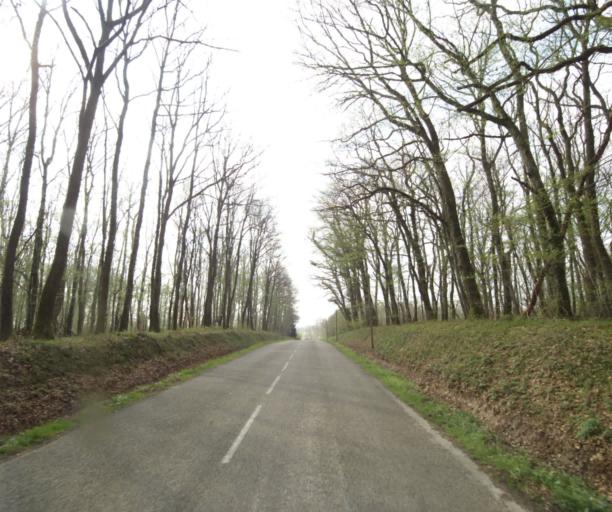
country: FR
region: Bourgogne
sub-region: Departement de Saone-et-Loire
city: Charolles
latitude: 46.4493
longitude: 4.2637
